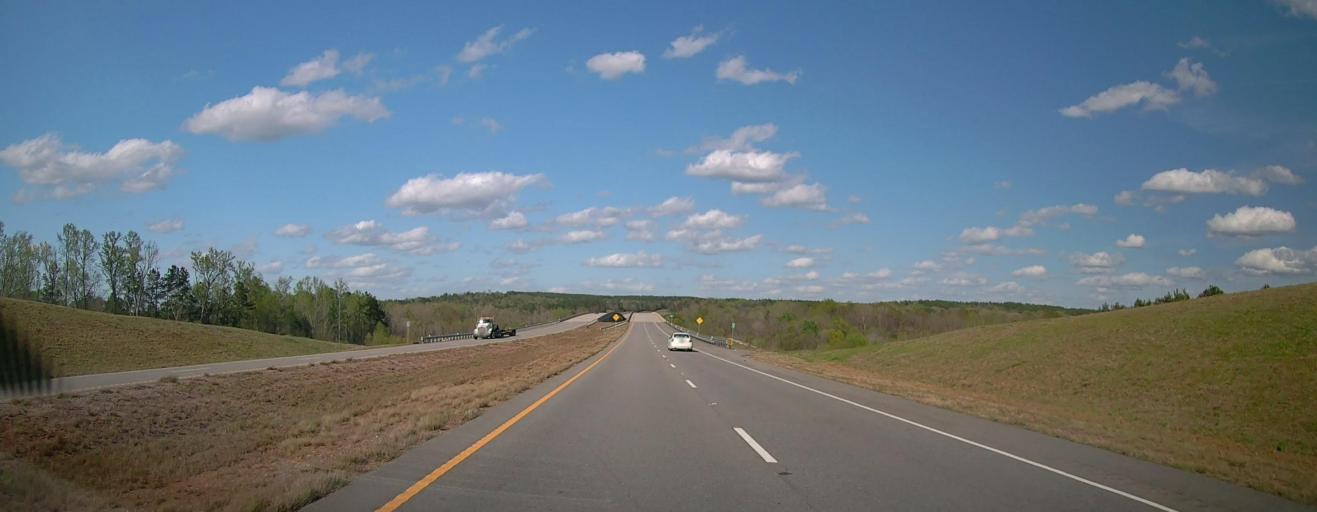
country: US
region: Georgia
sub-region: Baldwin County
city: Hardwick
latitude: 33.0209
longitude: -83.1887
